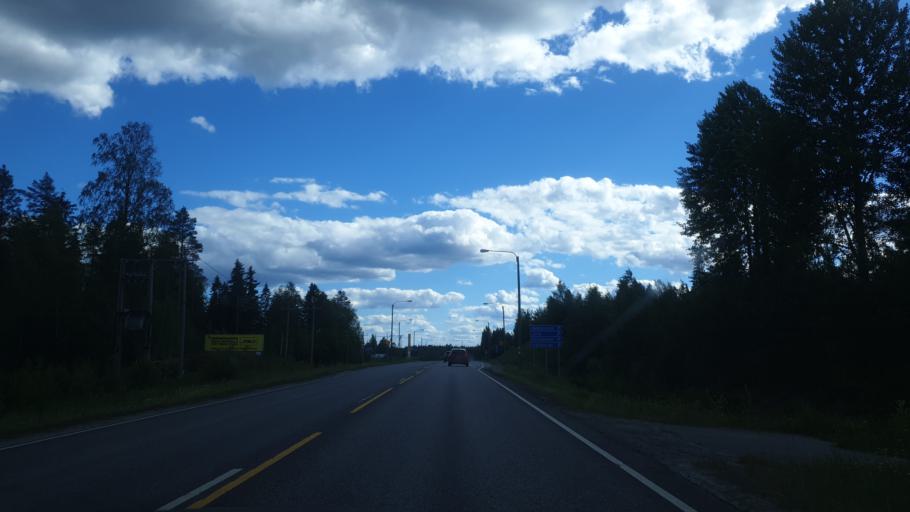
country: FI
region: Southern Savonia
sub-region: Pieksaemaeki
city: Juva
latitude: 61.9048
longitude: 27.8045
